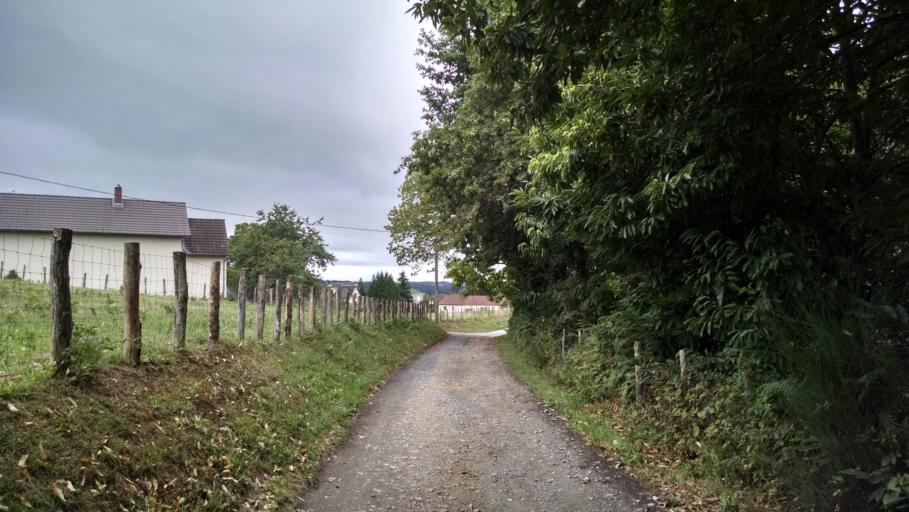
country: FR
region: Limousin
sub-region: Departement de la Haute-Vienne
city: Coussac-Bonneval
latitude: 45.5114
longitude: 1.3173
